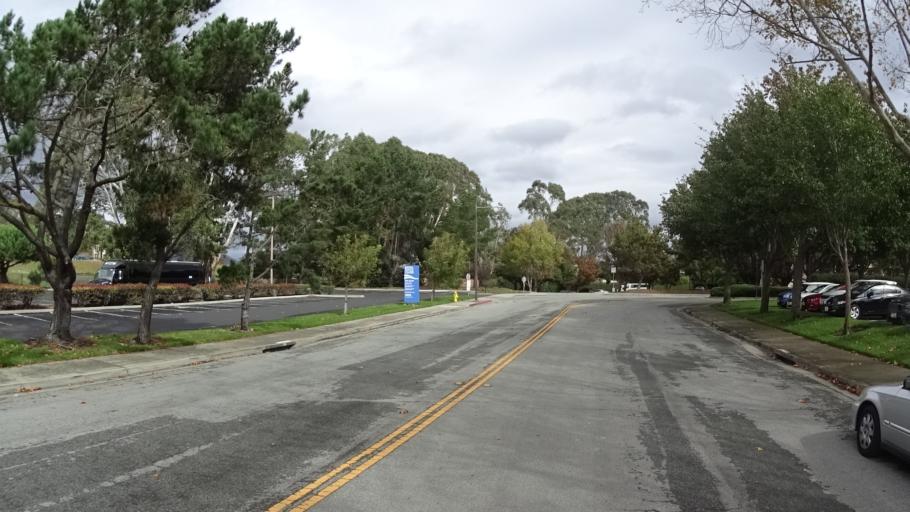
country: US
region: California
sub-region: San Mateo County
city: San Bruno
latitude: 37.6309
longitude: -122.4214
